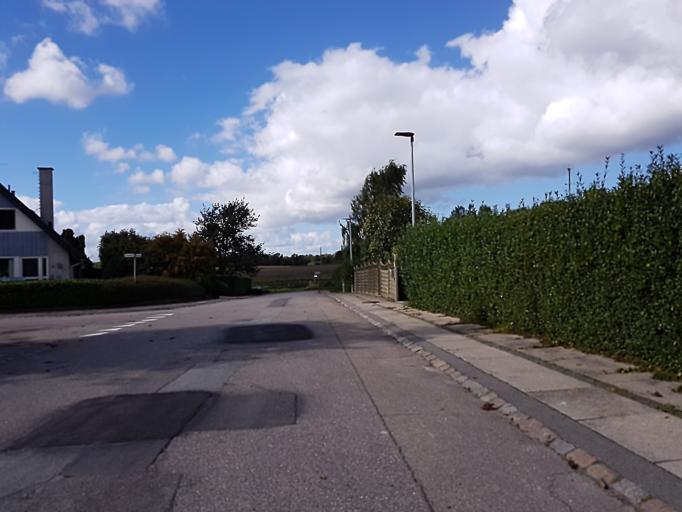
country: DK
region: Capital Region
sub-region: Egedal Kommune
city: Olstykke
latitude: 55.7882
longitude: 12.1345
